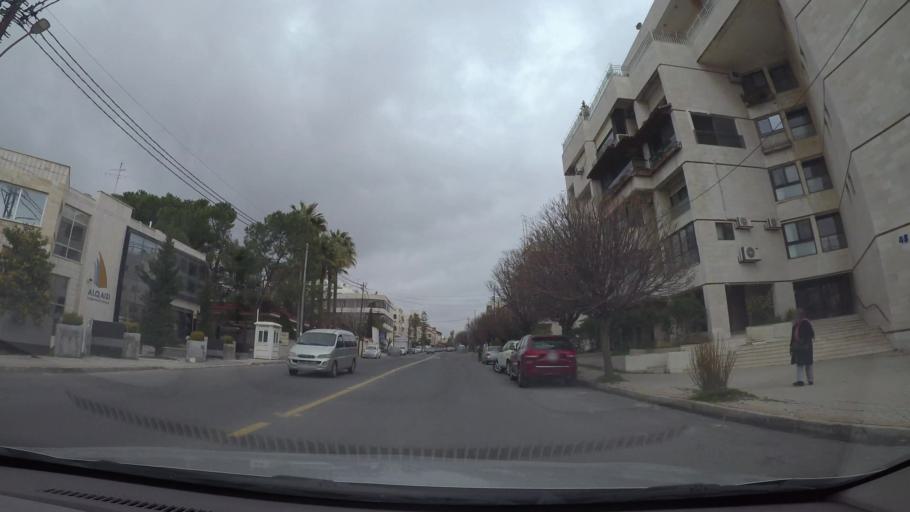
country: JO
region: Amman
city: Wadi as Sir
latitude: 31.9661
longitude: 35.8526
